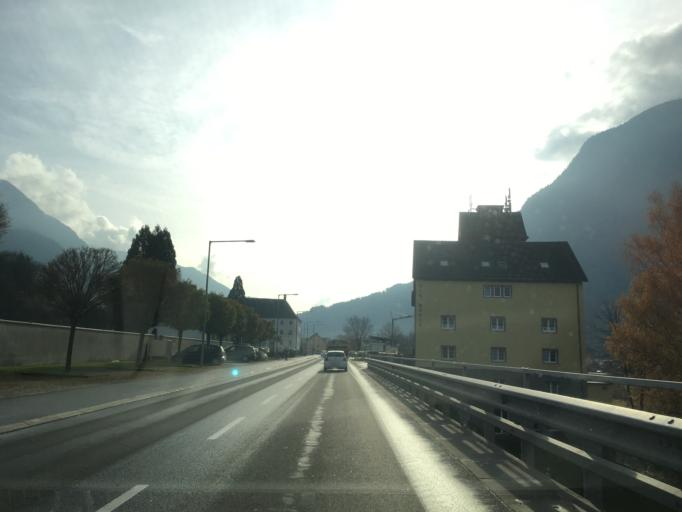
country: AT
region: Vorarlberg
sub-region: Politischer Bezirk Bludenz
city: Bludenz
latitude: 47.1476
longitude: 9.8280
